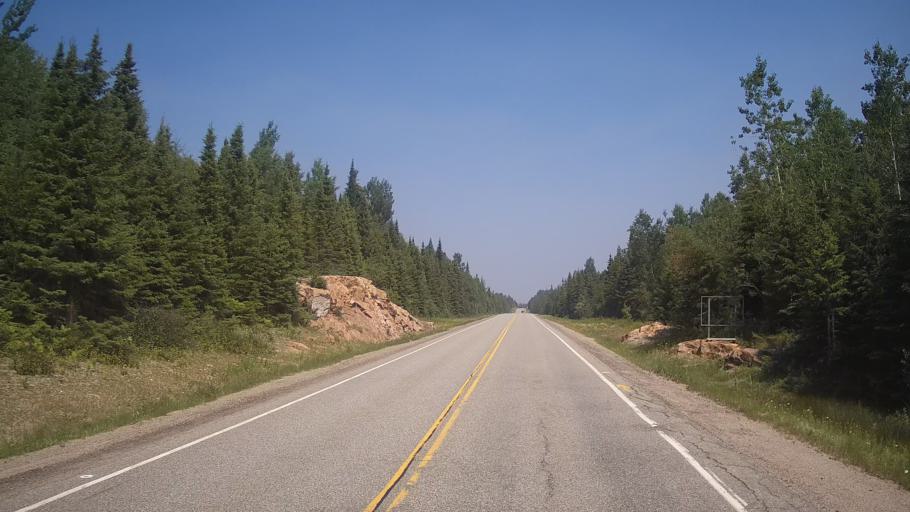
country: CA
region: Ontario
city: Timmins
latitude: 48.0352
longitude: -81.5824
